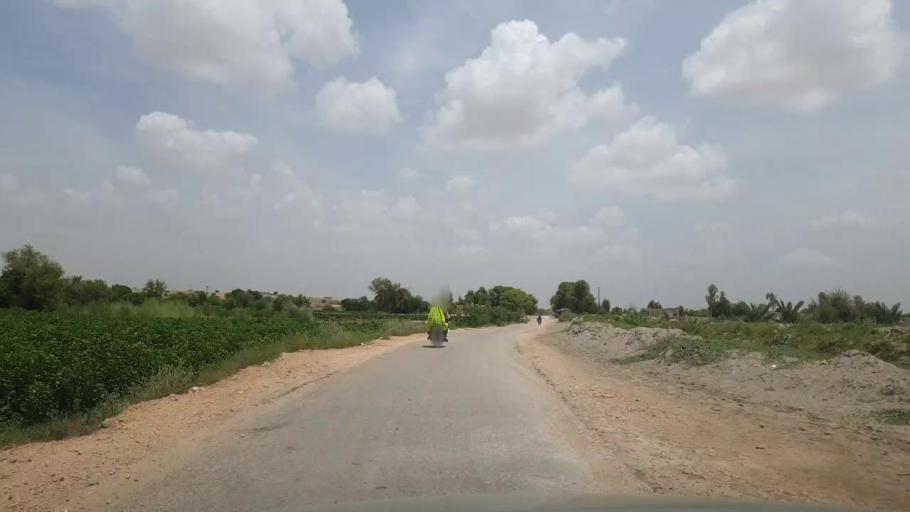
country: PK
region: Sindh
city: Kot Diji
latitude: 27.2013
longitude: 69.0566
